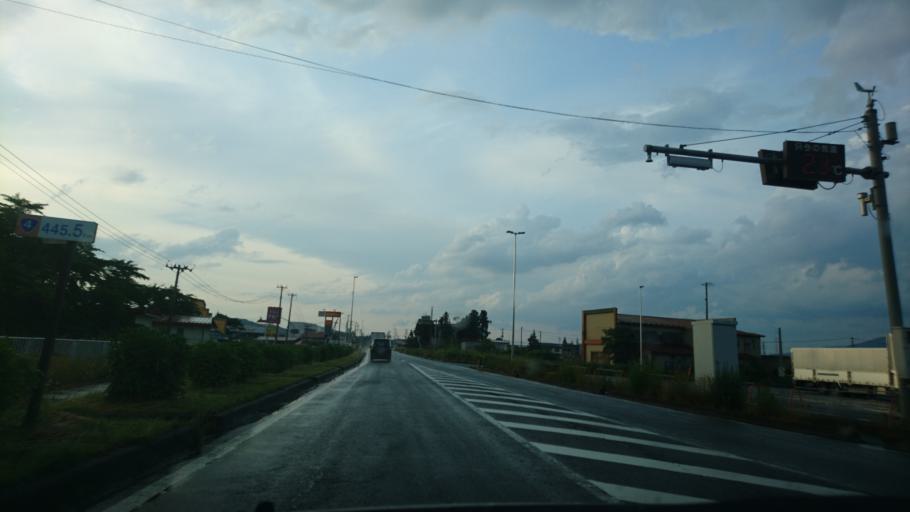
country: JP
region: Iwate
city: Ichinoseki
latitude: 38.9670
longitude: 141.1198
